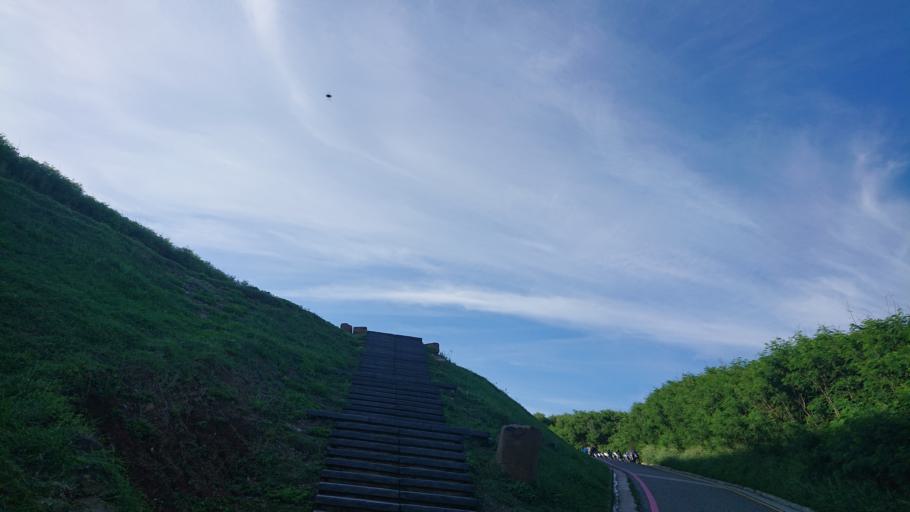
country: TW
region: Taiwan
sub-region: Penghu
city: Ma-kung
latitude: 23.5949
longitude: 119.5163
